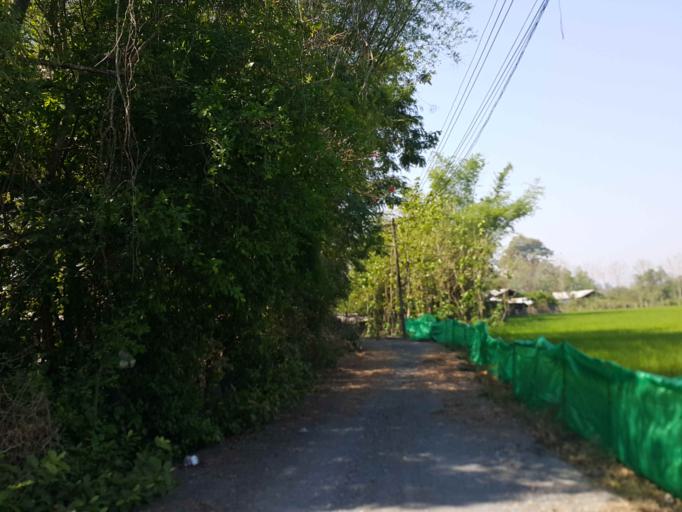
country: TH
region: Chiang Mai
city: San Kamphaeng
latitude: 18.7868
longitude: 99.0913
